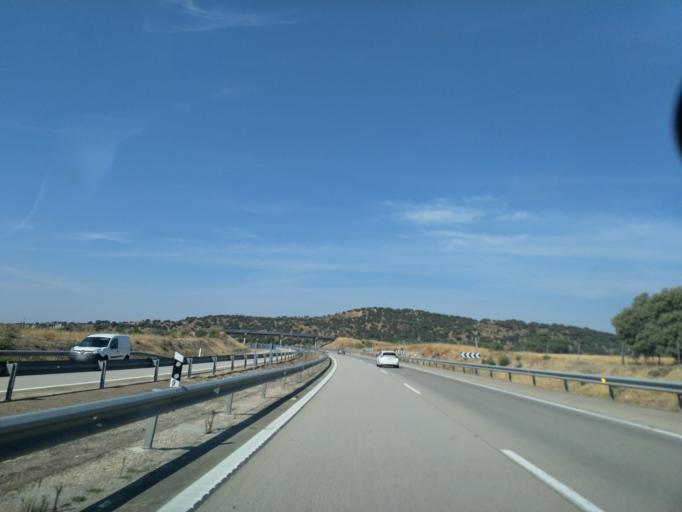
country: ES
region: Castille-La Mancha
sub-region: Province of Toledo
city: Cervera de los Montes
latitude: 40.0194
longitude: -4.7906
